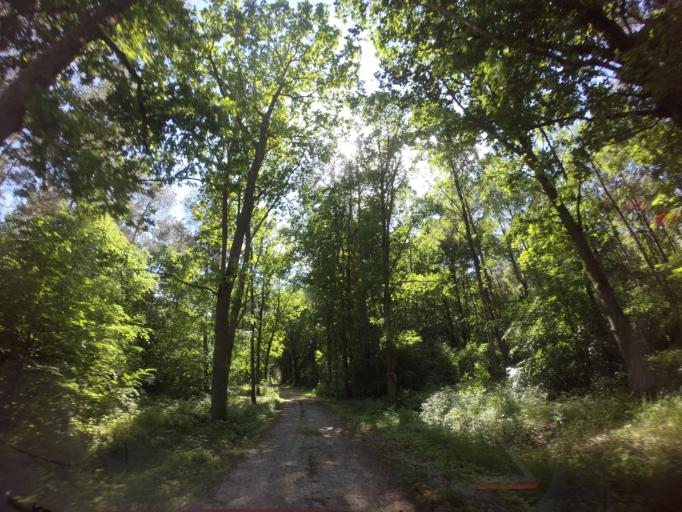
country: PL
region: West Pomeranian Voivodeship
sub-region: Powiat choszczenski
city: Drawno
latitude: 53.1860
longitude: 15.6760
